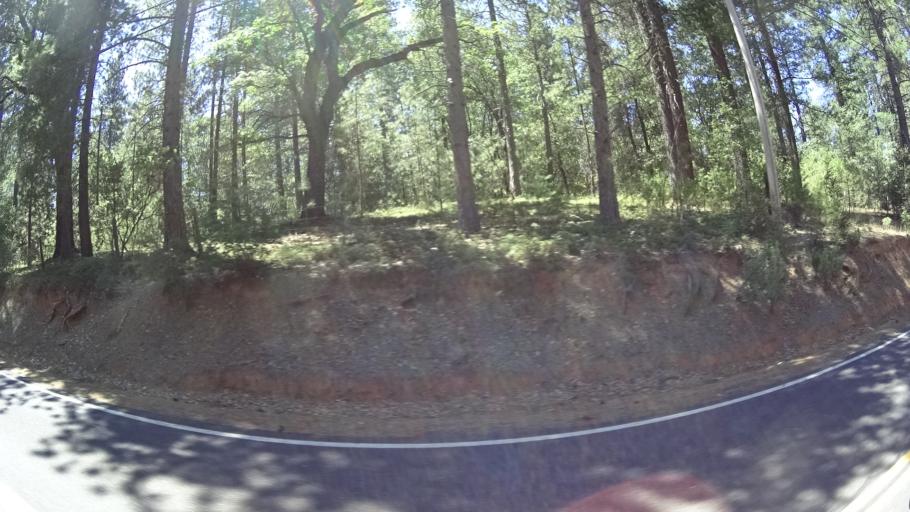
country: US
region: California
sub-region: Calaveras County
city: Mountain Ranch
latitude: 38.3144
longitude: -120.5205
